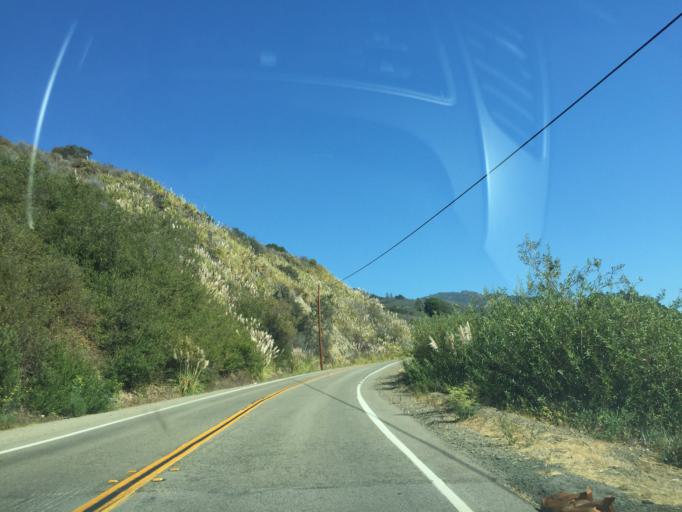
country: US
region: California
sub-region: Monterey County
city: Greenfield
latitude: 36.0209
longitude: -121.5488
